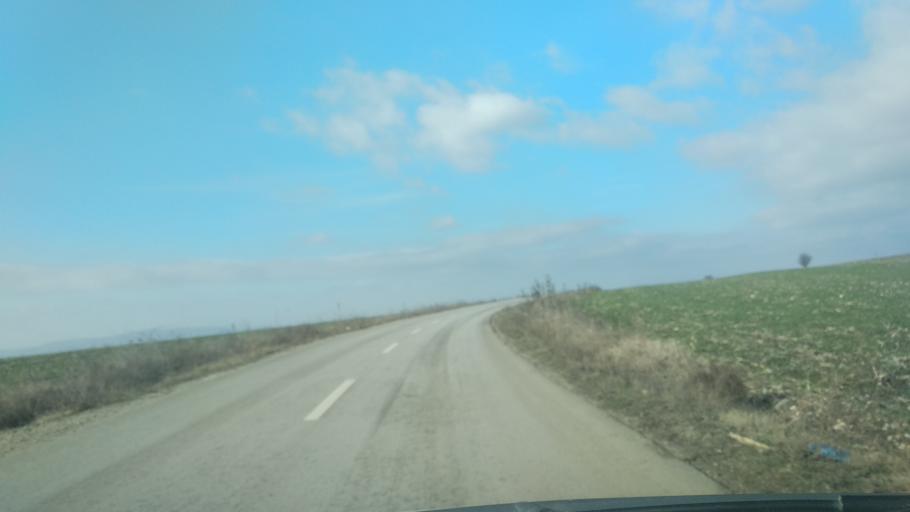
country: XK
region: Pristina
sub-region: Lipjan
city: Lipljan
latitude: 42.5567
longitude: 21.1751
